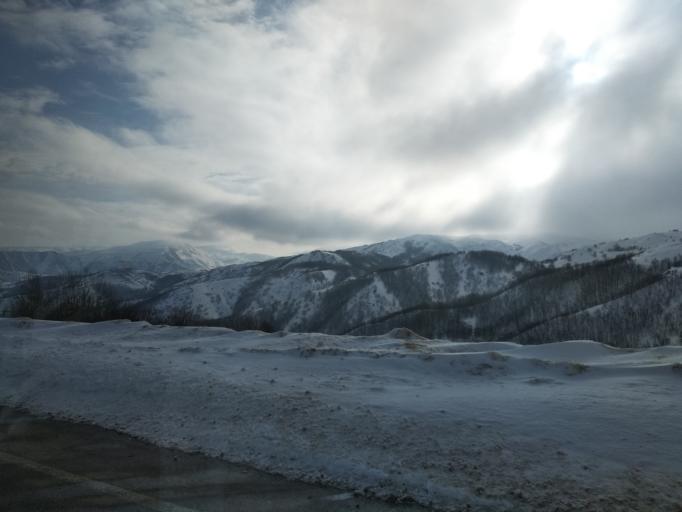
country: TR
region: Erzincan
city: Catalarmut
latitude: 39.8951
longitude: 39.3826
